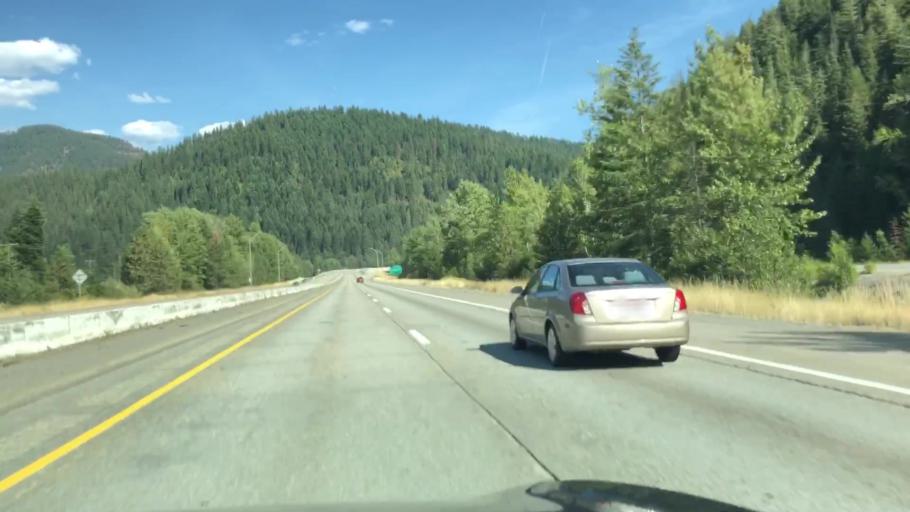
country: US
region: Idaho
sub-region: Shoshone County
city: Osburn
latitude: 47.4912
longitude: -115.9642
